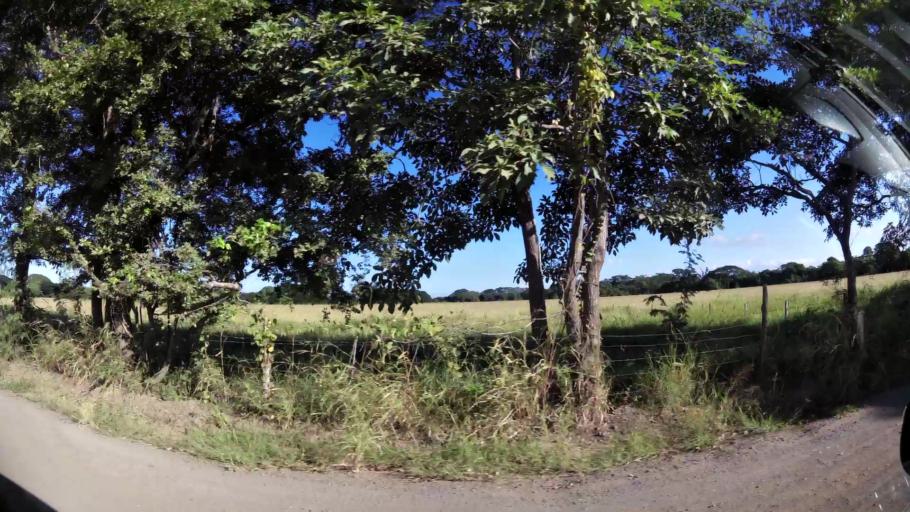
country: CR
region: Guanacaste
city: Sardinal
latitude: 10.4857
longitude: -85.5754
